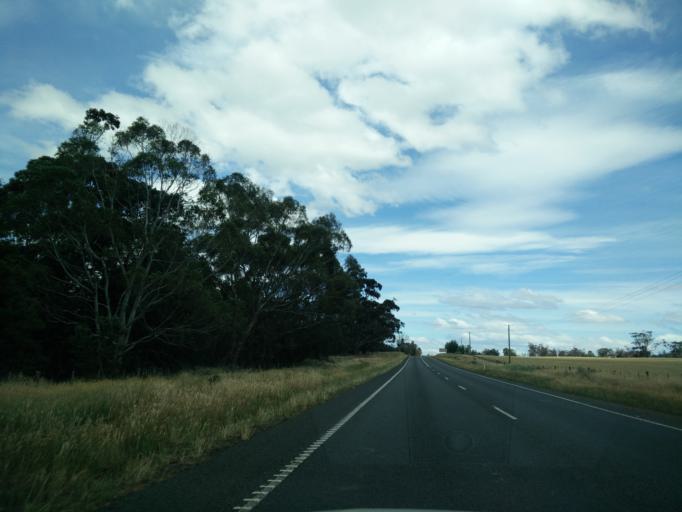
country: AU
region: Tasmania
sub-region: Northern Midlands
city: Evandale
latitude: -41.6959
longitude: 147.2872
